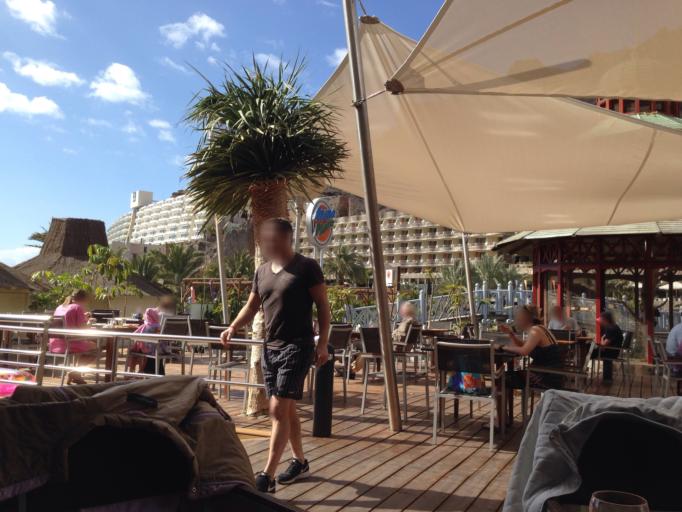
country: ES
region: Canary Islands
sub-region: Provincia de Las Palmas
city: Puerto Rico
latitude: 27.8169
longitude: -15.7516
